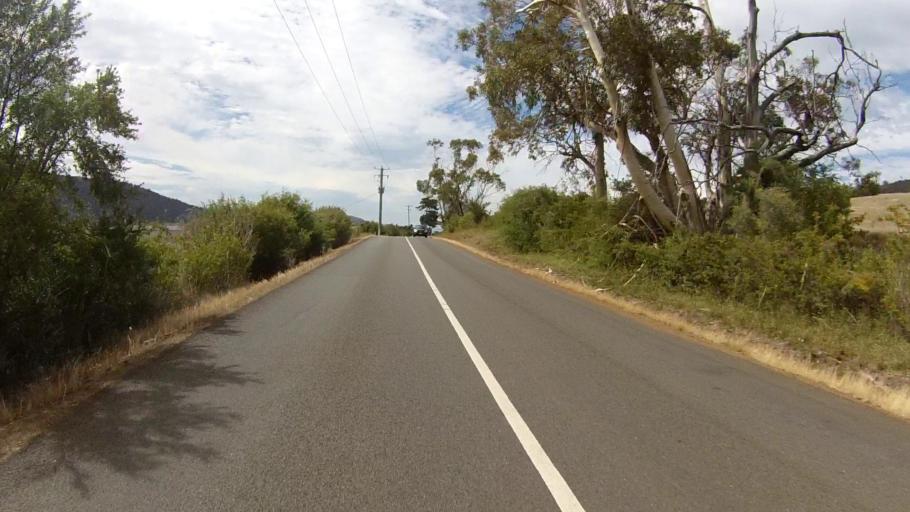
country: AU
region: Tasmania
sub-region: Brighton
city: Old Beach
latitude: -42.7050
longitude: 147.3667
